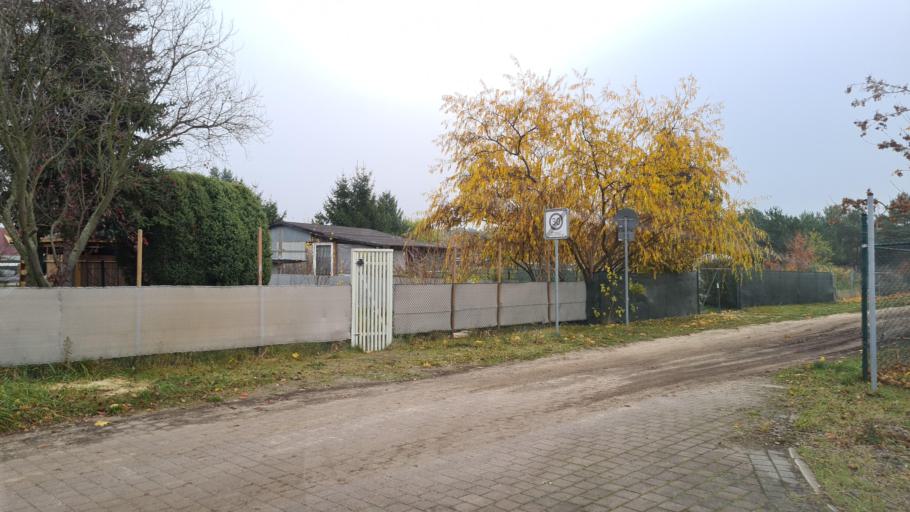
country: DE
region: Brandenburg
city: Golzow
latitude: 52.3484
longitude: 12.6307
